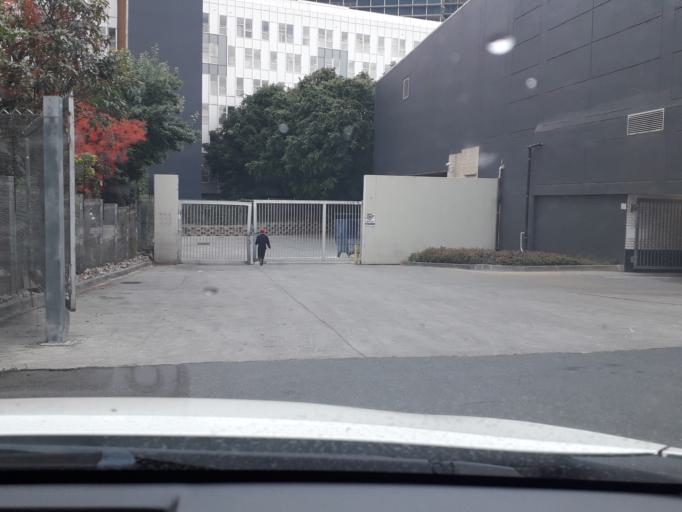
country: ZA
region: Gauteng
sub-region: City of Johannesburg Metropolitan Municipality
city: Johannesburg
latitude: -26.0998
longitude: 28.0483
